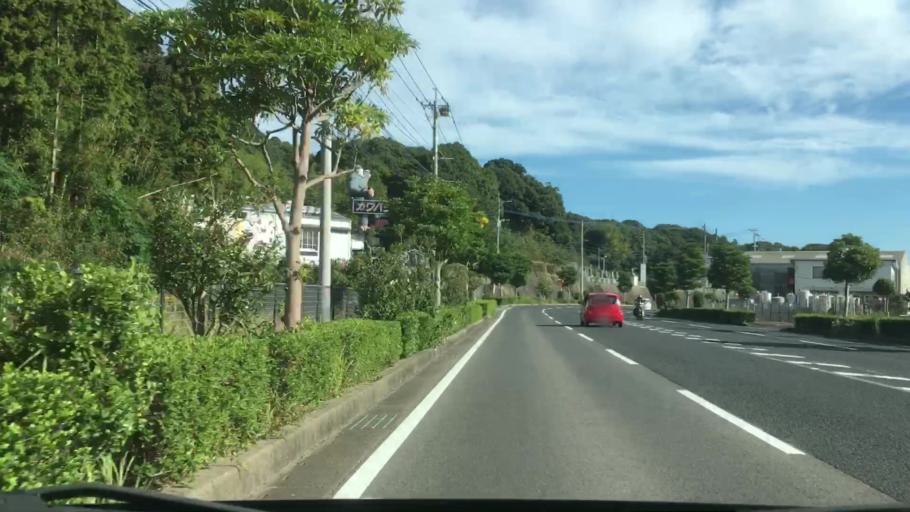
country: JP
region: Nagasaki
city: Sasebo
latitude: 33.1123
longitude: 129.7871
